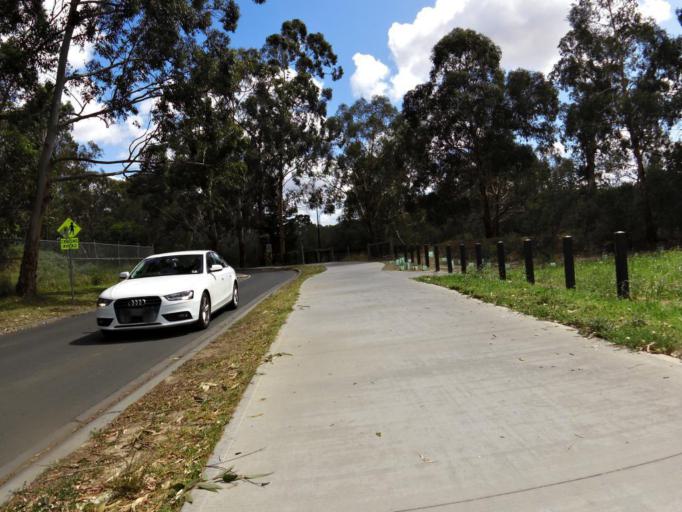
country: AU
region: Victoria
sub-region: Nillumbik
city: Eltham
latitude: -37.7249
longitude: 145.1435
